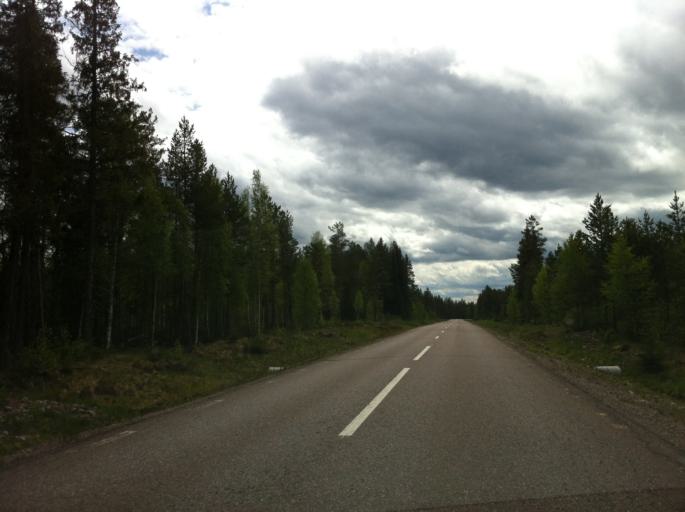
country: NO
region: Hedmark
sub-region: Trysil
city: Innbygda
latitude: 61.5355
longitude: 13.0820
